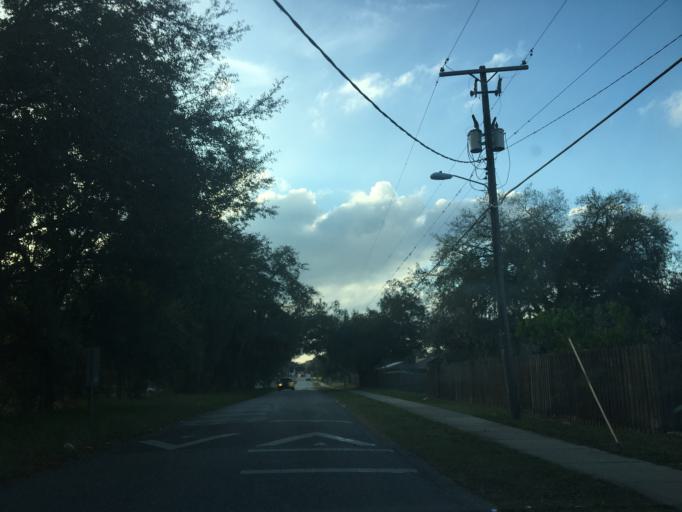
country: US
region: Florida
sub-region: Hillsborough County
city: Temple Terrace
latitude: 28.0253
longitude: -82.4074
